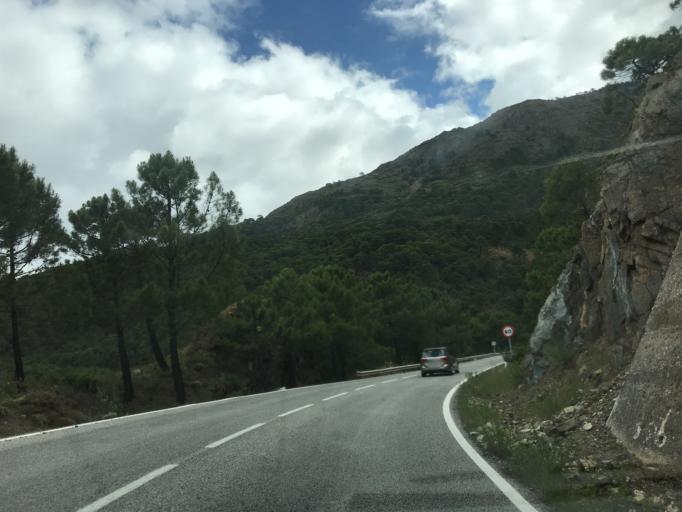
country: ES
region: Andalusia
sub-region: Provincia de Malaga
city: Benahavis
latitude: 36.5656
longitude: -5.0596
